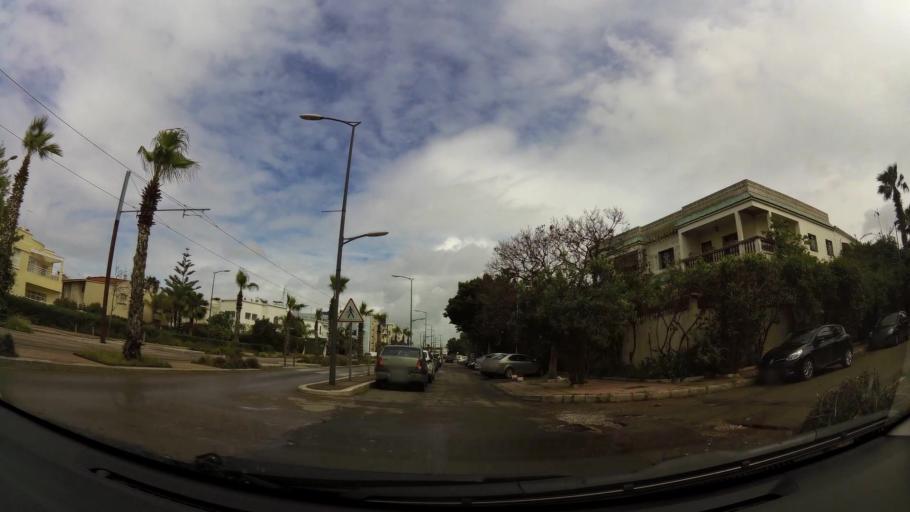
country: MA
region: Grand Casablanca
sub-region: Casablanca
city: Casablanca
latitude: 33.5408
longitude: -7.6458
